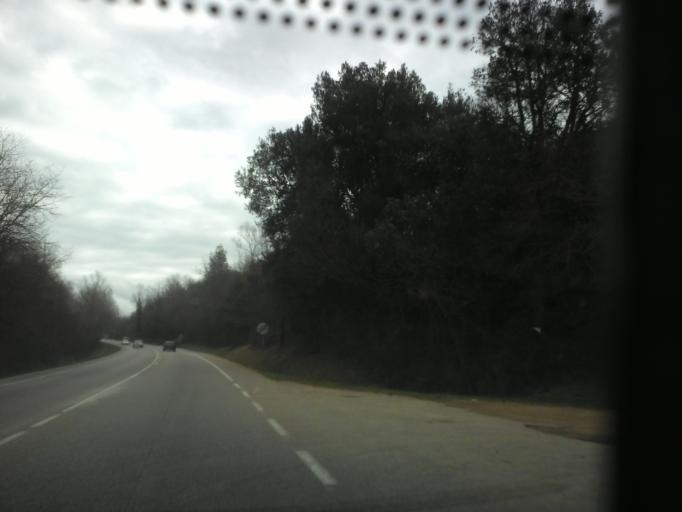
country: ES
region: Catalonia
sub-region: Provincia de Girona
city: Quart d'Onyar
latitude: 41.9372
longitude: 2.8261
